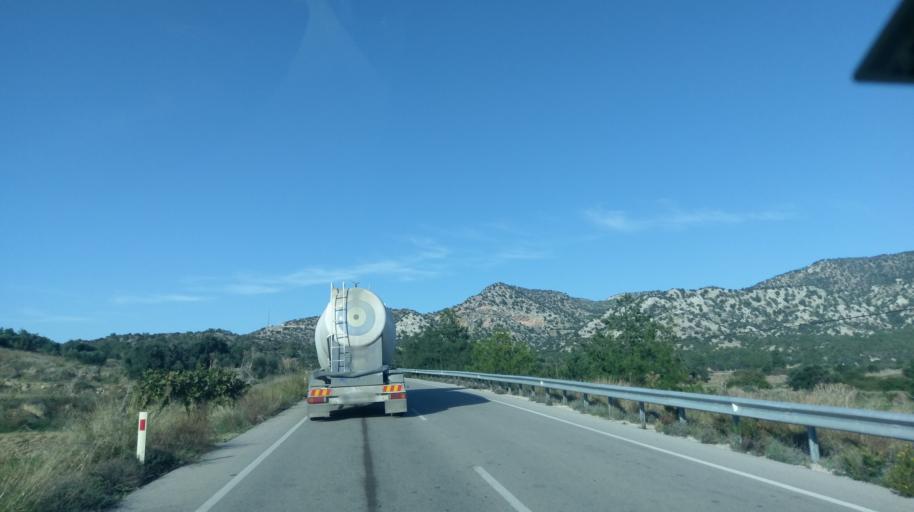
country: CY
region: Ammochostos
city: Lefkonoiko
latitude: 35.3337
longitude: 33.7201
